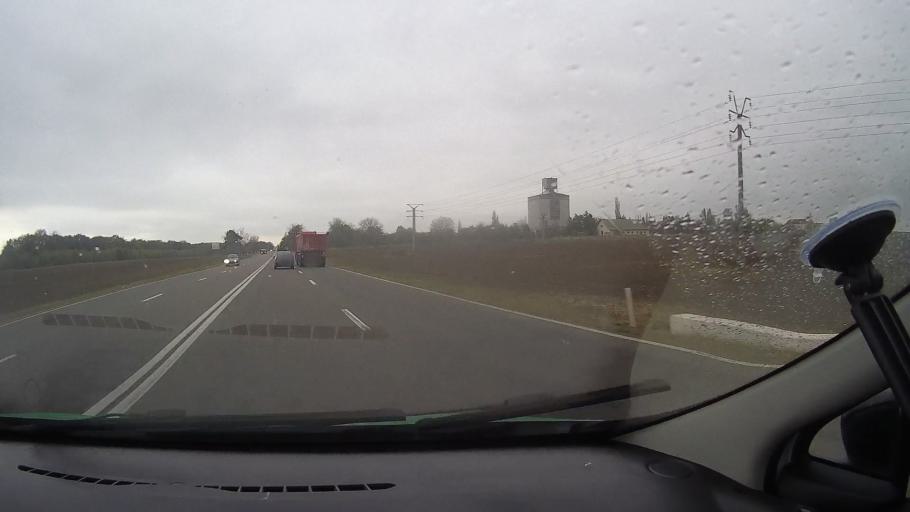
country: RO
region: Constanta
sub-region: Comuna Valu lui Traian
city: Valu lui Traian
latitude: 44.1655
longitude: 28.5157
